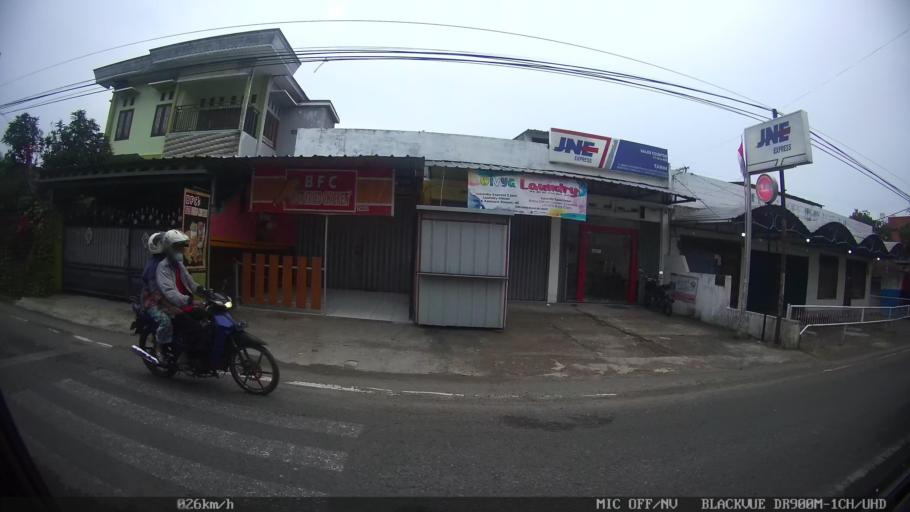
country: ID
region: Lampung
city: Bandarlampung
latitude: -5.4089
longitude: 105.2487
